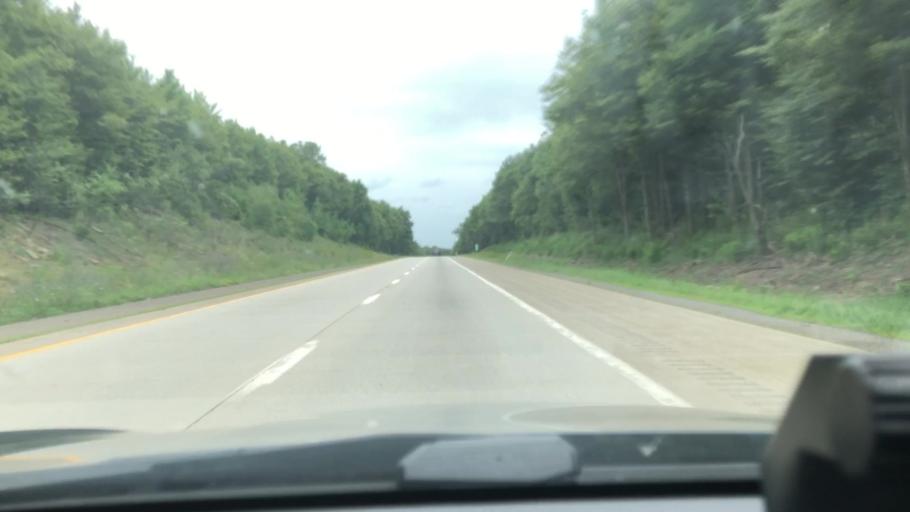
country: US
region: Pennsylvania
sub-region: Monroe County
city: Mount Pocono
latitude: 41.1500
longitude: -75.4089
